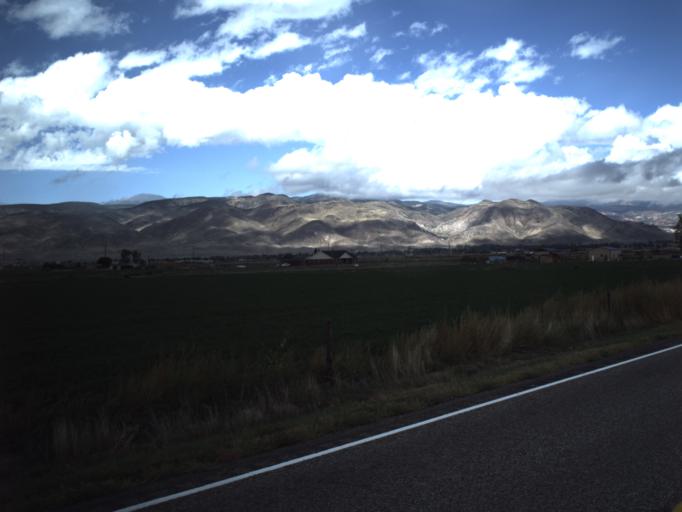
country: US
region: Utah
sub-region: Sevier County
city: Monroe
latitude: 38.6467
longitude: -112.1215
